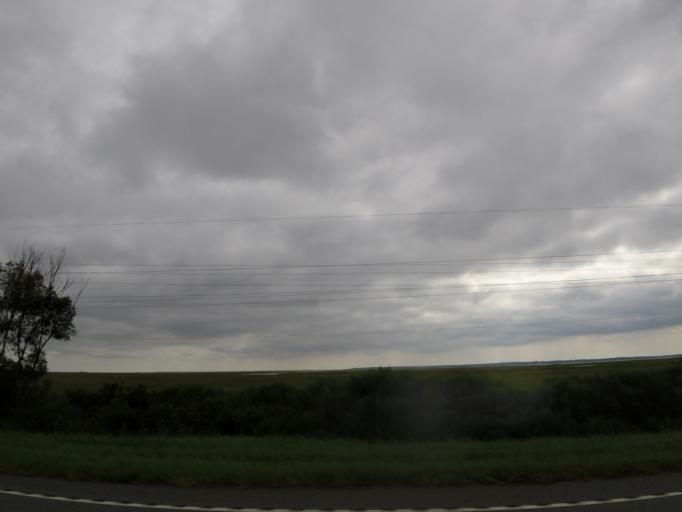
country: US
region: Georgia
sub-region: Glynn County
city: Brunswick
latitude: 31.0700
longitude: -81.4614
